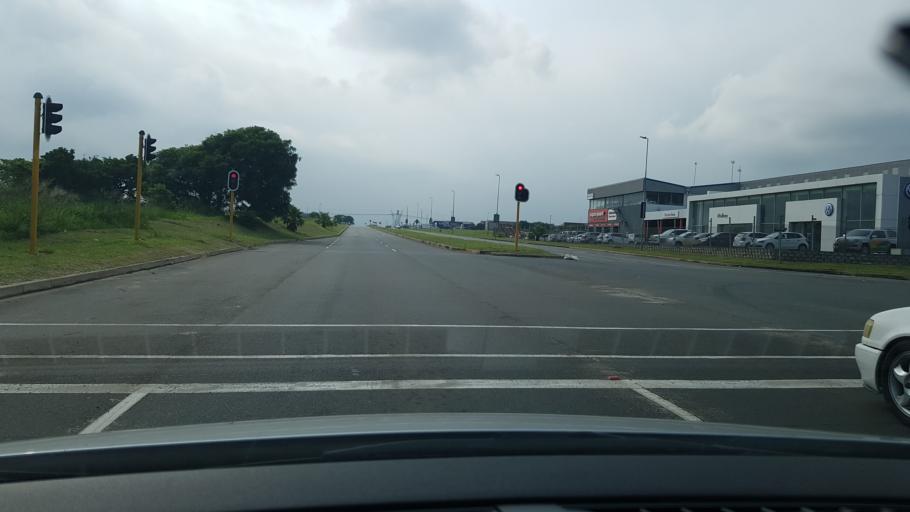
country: ZA
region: KwaZulu-Natal
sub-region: uThungulu District Municipality
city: Richards Bay
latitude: -28.7588
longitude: 32.0486
